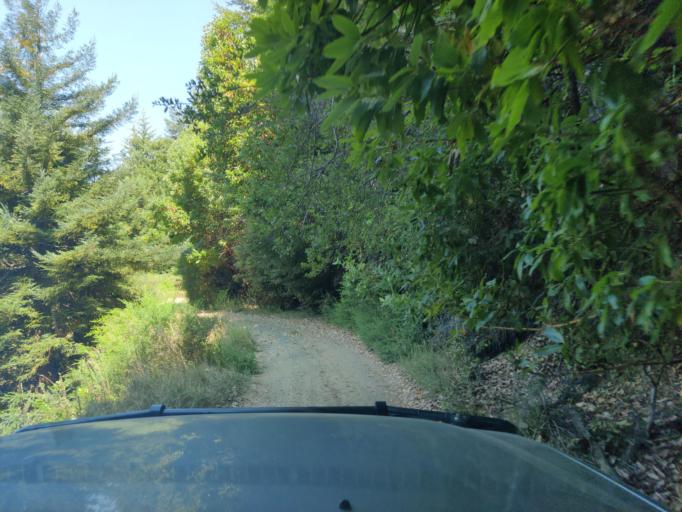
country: US
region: California
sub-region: Humboldt County
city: Redway
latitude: 39.9027
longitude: -123.8884
